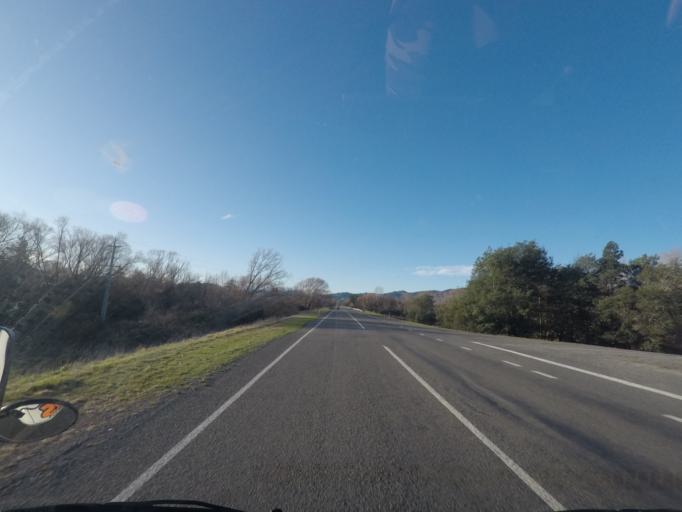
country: NZ
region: Canterbury
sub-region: Kaikoura District
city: Kaikoura
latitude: -42.7252
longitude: 173.2809
